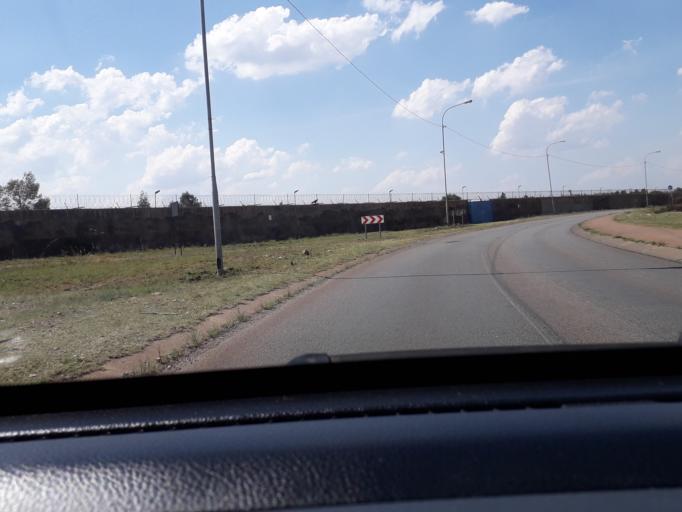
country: ZA
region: Gauteng
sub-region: City of Tshwane Metropolitan Municipality
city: Centurion
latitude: -25.8463
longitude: 28.2268
